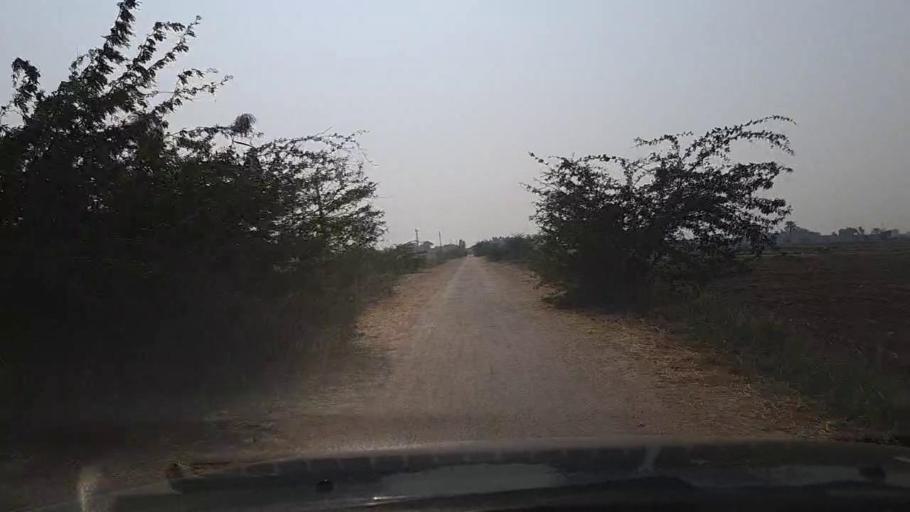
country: PK
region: Sindh
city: Thatta
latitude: 24.7956
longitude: 67.8746
